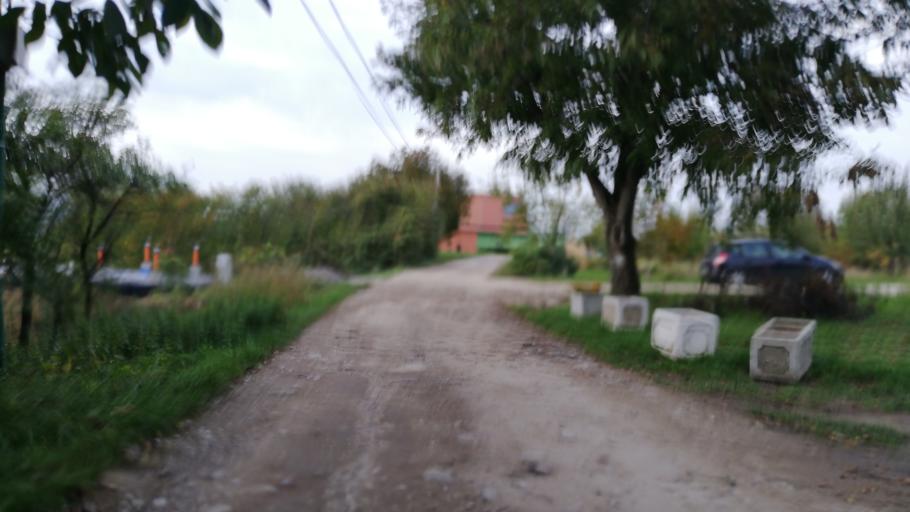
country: SK
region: Trnavsky
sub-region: Okres Skalica
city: Skalica
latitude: 48.8252
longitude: 17.2341
